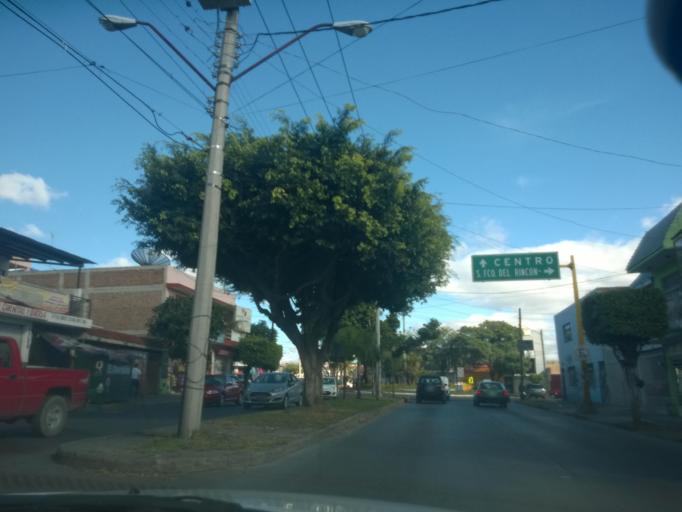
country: MX
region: Guanajuato
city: Leon
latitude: 21.1158
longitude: -101.6968
